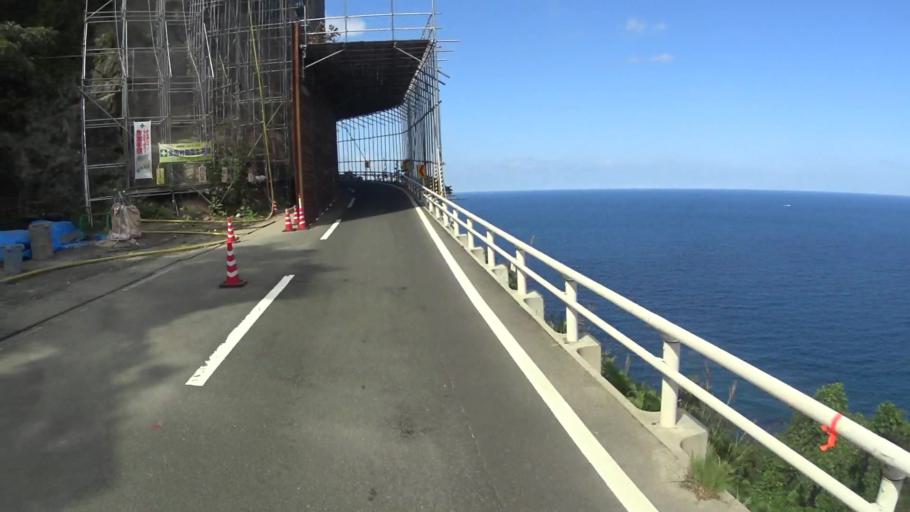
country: JP
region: Kyoto
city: Miyazu
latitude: 35.7665
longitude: 135.2343
